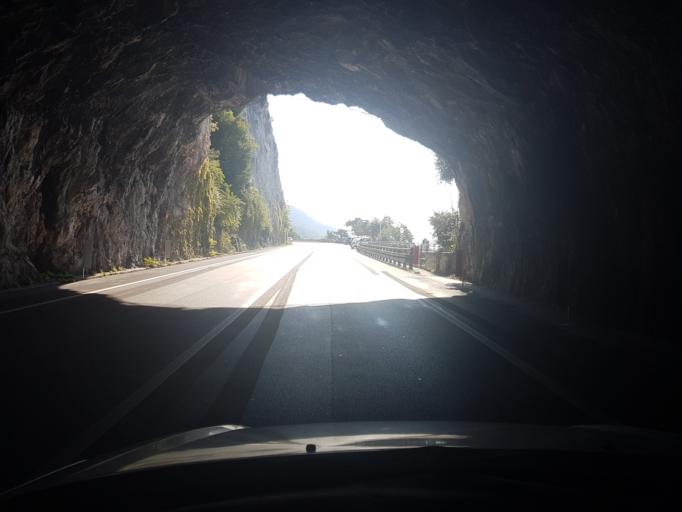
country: IT
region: Friuli Venezia Giulia
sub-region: Provincia di Trieste
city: Aurisina
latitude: 45.7444
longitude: 13.6652
